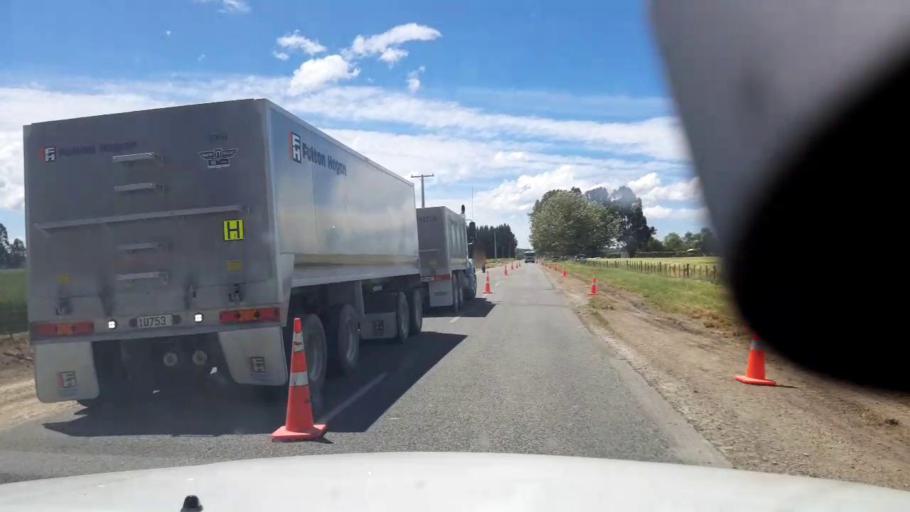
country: NZ
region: Canterbury
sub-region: Timaru District
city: Pleasant Point
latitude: -44.2790
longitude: 171.2476
